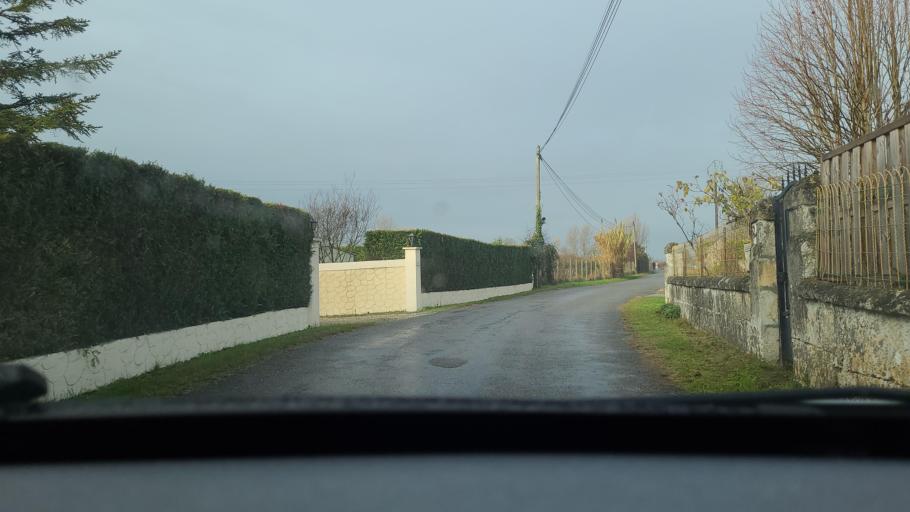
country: FR
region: Aquitaine
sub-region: Departement de la Gironde
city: Marcamps
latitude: 45.0335
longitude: -0.4854
